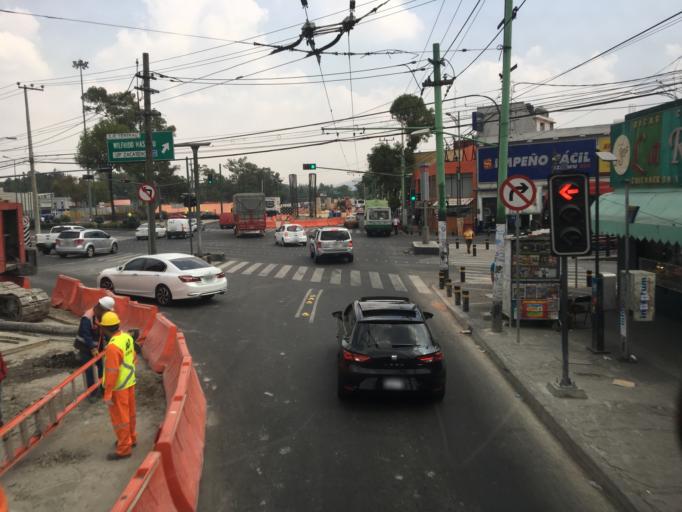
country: MX
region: Mexico
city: Colonia Lindavista
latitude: 19.4928
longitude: -99.1457
